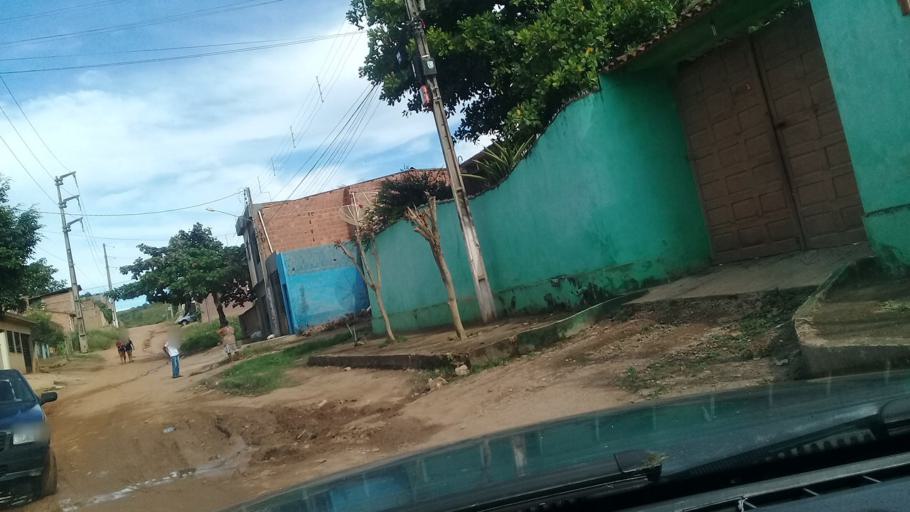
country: BR
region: Pernambuco
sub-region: Vitoria De Santo Antao
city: Vitoria de Santo Antao
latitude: -8.1305
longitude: -35.2924
